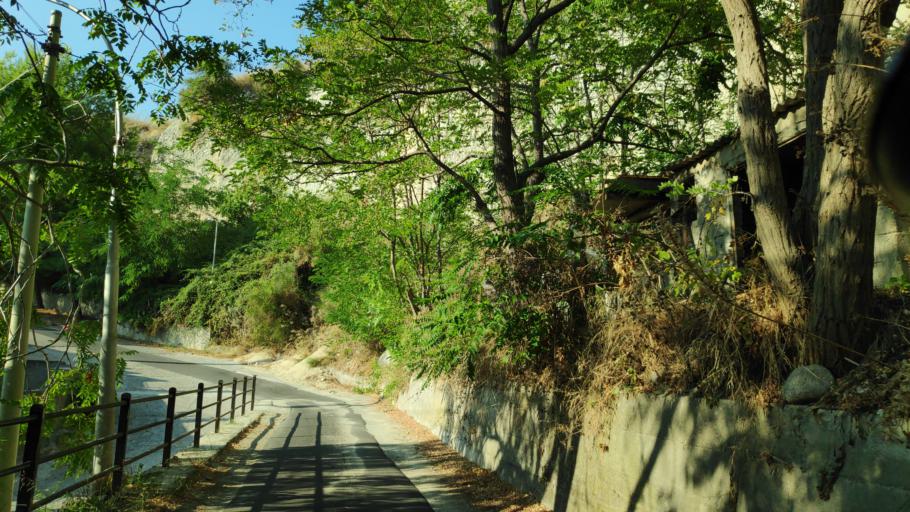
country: IT
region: Calabria
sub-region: Provincia di Catanzaro
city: Guardavalle
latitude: 38.5074
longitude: 16.5043
